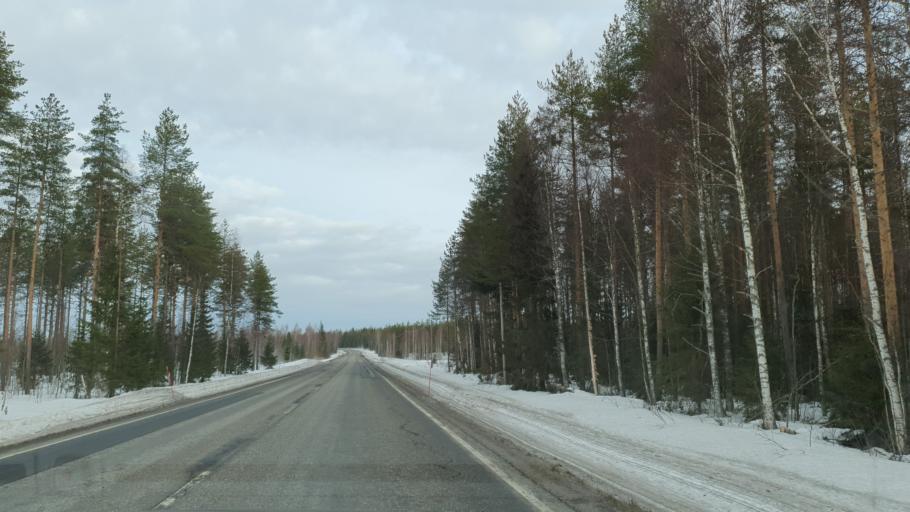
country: FI
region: Kainuu
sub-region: Kajaani
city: Vuokatti
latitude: 64.1945
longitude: 28.1733
